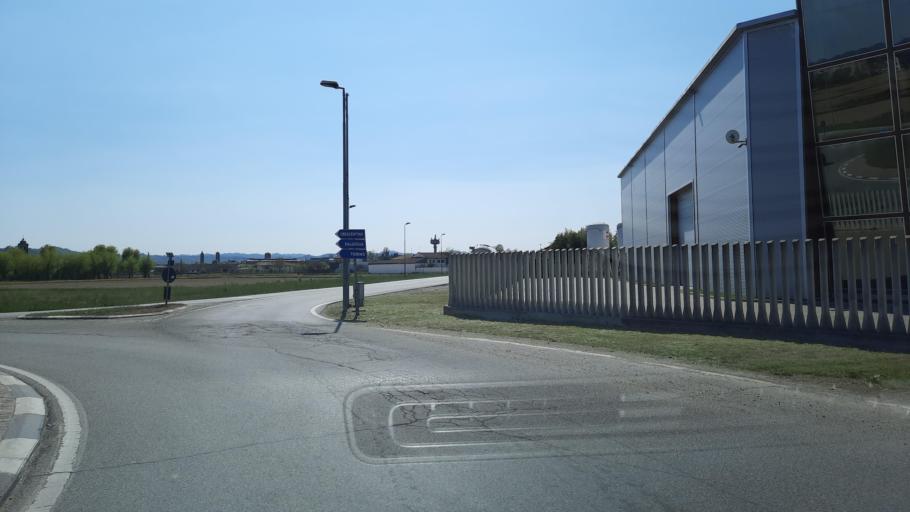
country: IT
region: Piedmont
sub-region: Provincia di Vercelli
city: Crescentino
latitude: 45.2011
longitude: 8.1098
